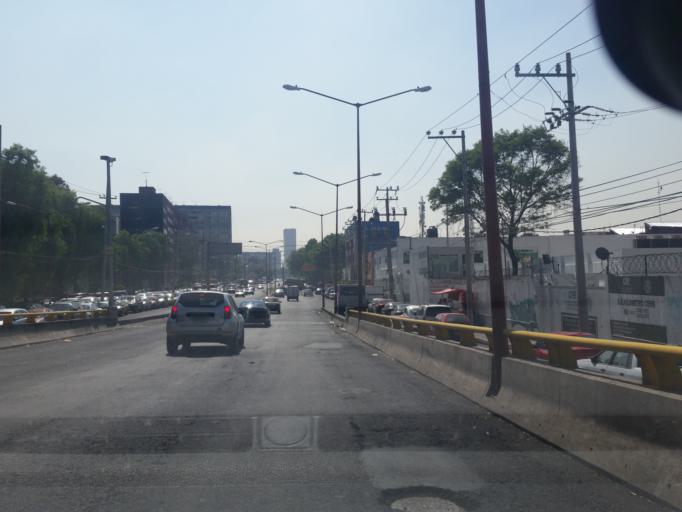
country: MX
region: Mexico City
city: Cuauhtemoc
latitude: 19.4535
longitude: -99.1491
